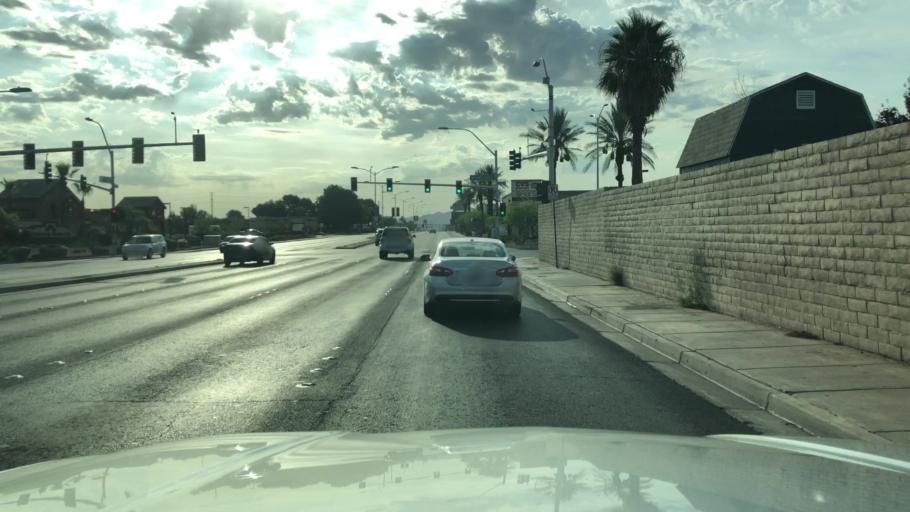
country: US
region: Nevada
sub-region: Clark County
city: Whitney
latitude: 36.0636
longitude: -115.0533
